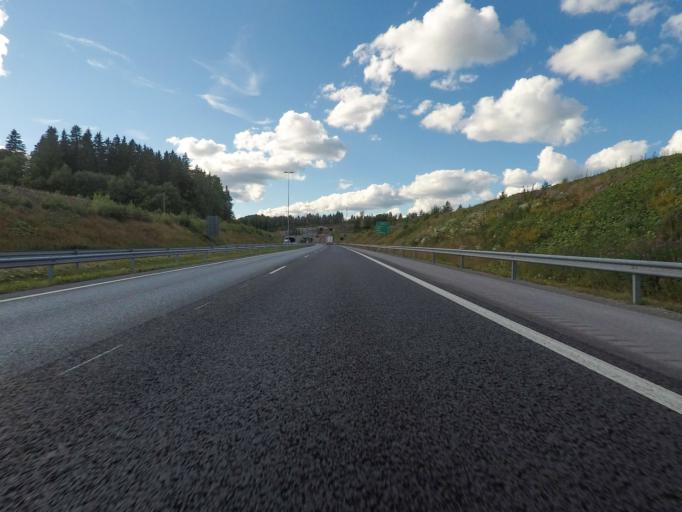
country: FI
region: Uusimaa
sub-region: Helsinki
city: Lohja
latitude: 60.2983
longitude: 24.0585
